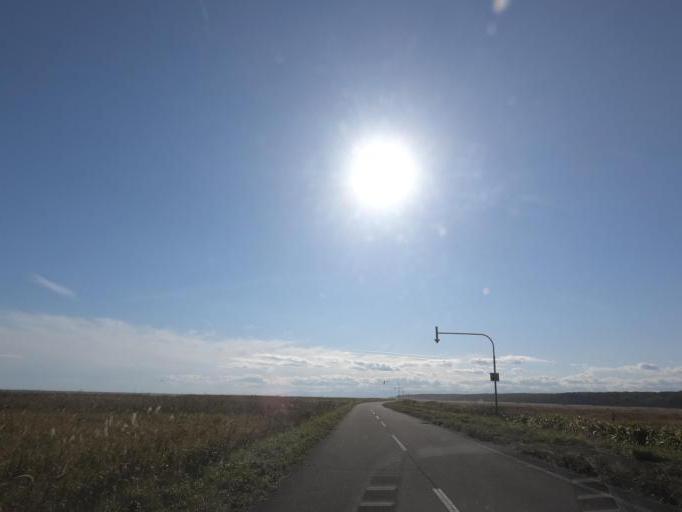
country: JP
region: Hokkaido
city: Obihiro
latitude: 42.5950
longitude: 143.5450
